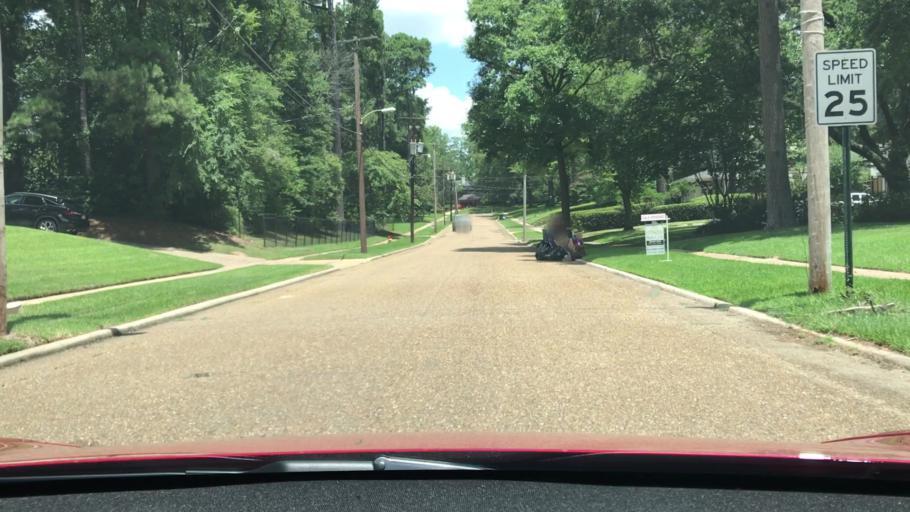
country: US
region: Louisiana
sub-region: Bossier Parish
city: Bossier City
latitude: 32.4569
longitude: -93.7538
